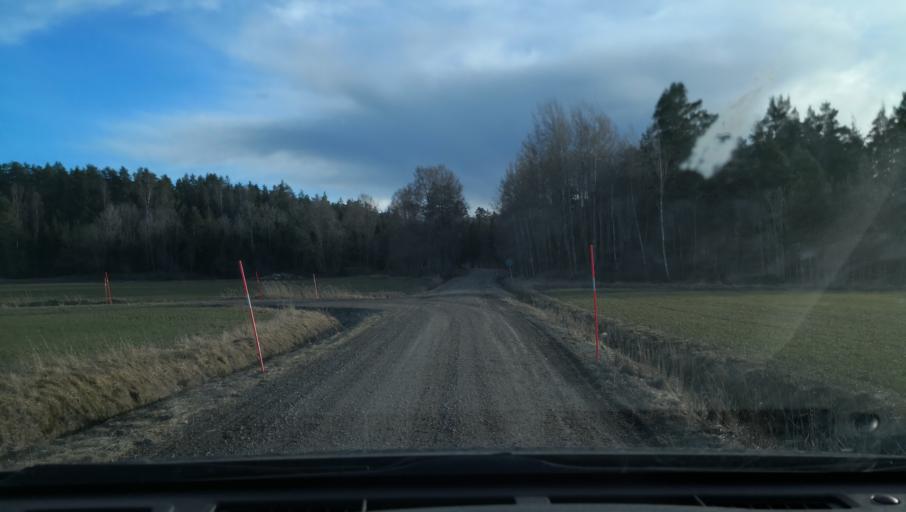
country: SE
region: Vaestmanland
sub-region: Arboga Kommun
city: Arboga
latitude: 59.4450
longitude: 15.7527
